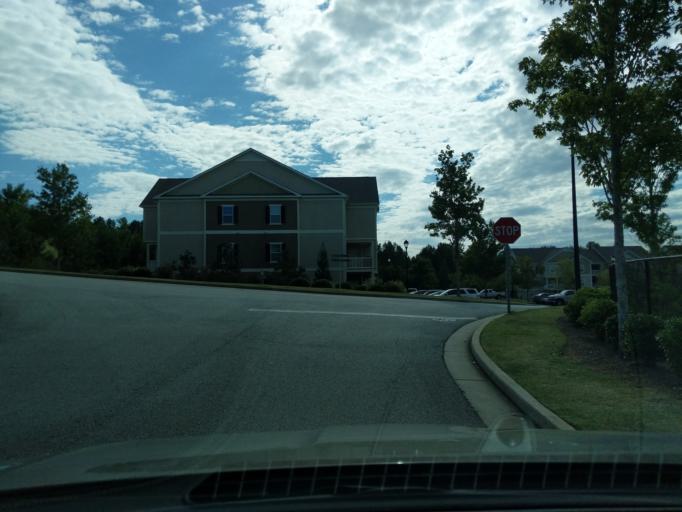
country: US
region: Georgia
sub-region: Columbia County
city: Grovetown
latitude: 33.4803
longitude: -82.2036
